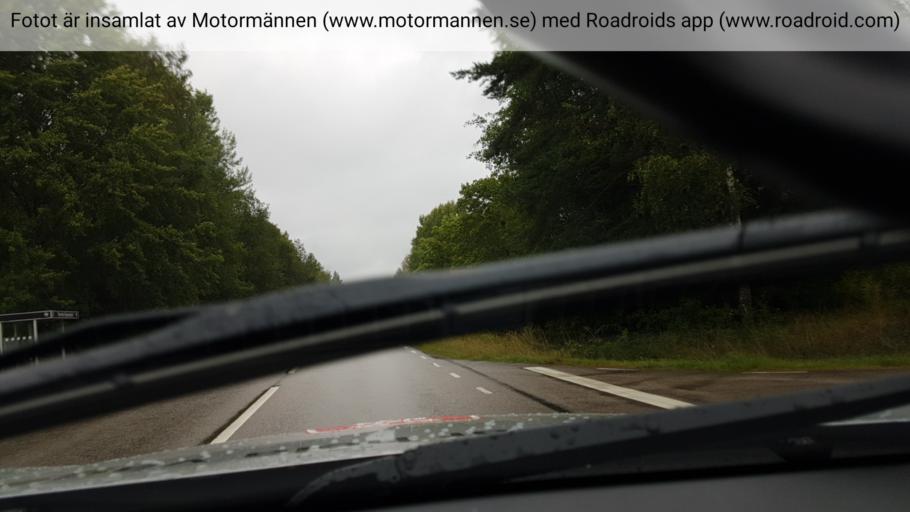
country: SE
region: Vaestra Goetaland
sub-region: Bengtsfors Kommun
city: Billingsfors
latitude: 58.9246
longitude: 12.2166
